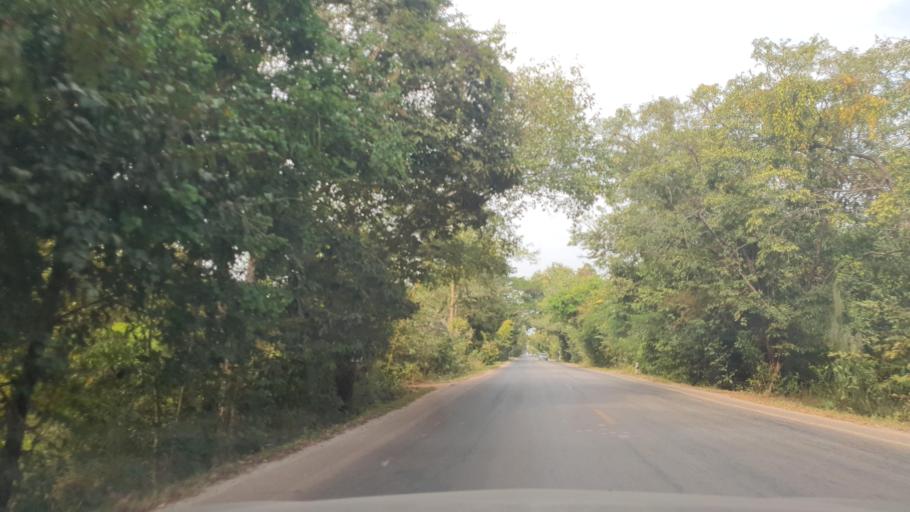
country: TH
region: Changwat Bueng Kan
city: Bung Khla
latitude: 18.2055
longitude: 104.0492
